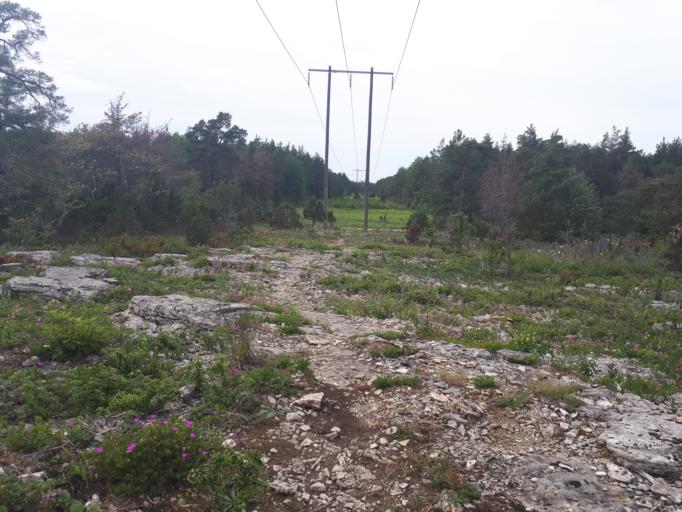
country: SE
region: Gotland
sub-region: Gotland
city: Visby
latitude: 57.6029
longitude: 18.3060
